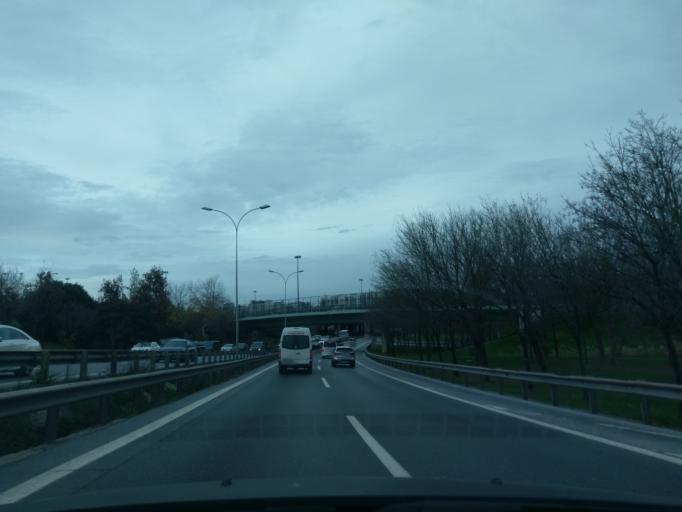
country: TR
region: Istanbul
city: Bahcelievler
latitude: 40.9911
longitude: 28.8184
